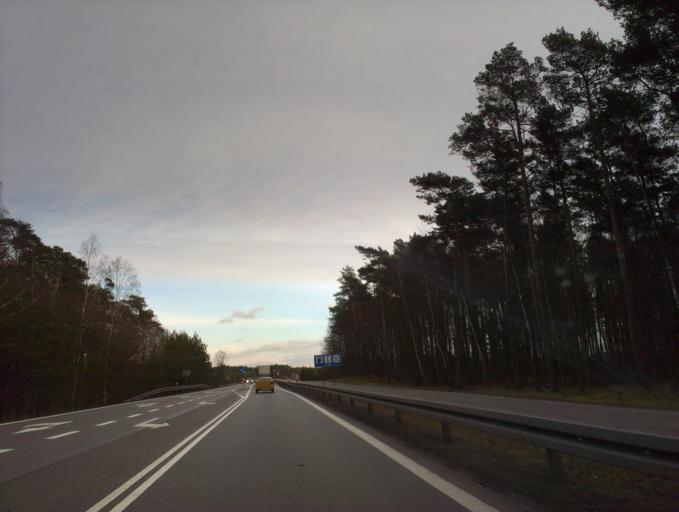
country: PL
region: Kujawsko-Pomorskie
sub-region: Powiat lipnowski
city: Skepe
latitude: 52.8771
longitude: 19.3406
